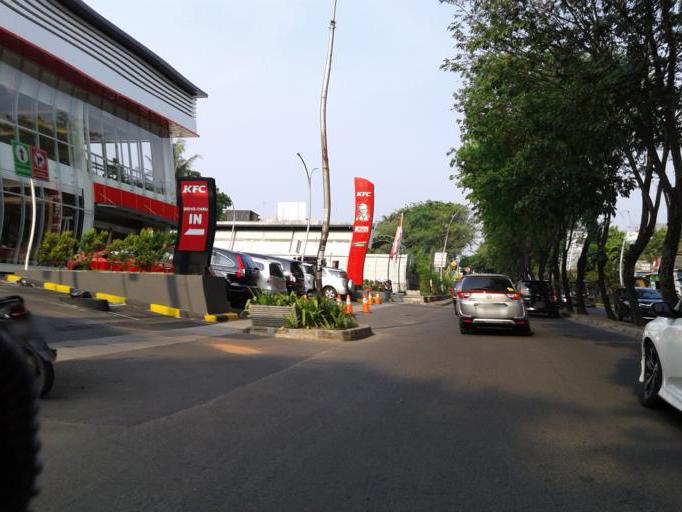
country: ID
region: Banten
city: South Tangerang
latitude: -6.2802
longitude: 106.7156
